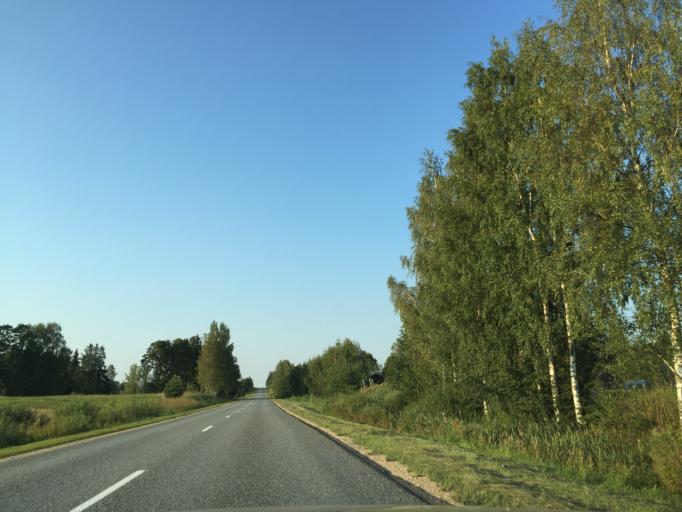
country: LV
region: Limbazu Rajons
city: Limbazi
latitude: 57.5648
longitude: 24.7671
